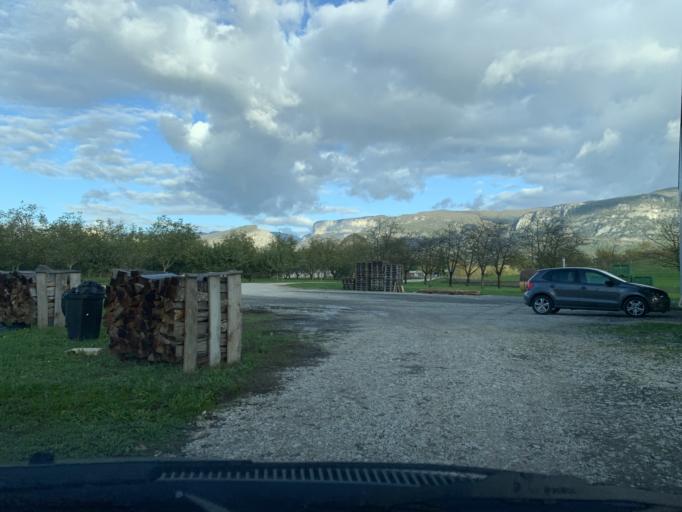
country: FR
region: Rhone-Alpes
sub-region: Departement de la Drome
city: Saint-Jean-en-Royans
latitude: 45.0306
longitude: 5.3004
